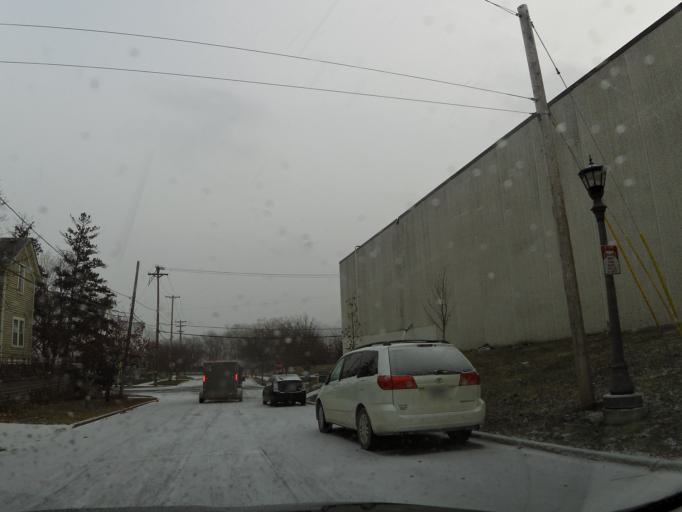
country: US
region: Minnesota
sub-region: Dakota County
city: West Saint Paul
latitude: 44.9287
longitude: -93.1216
